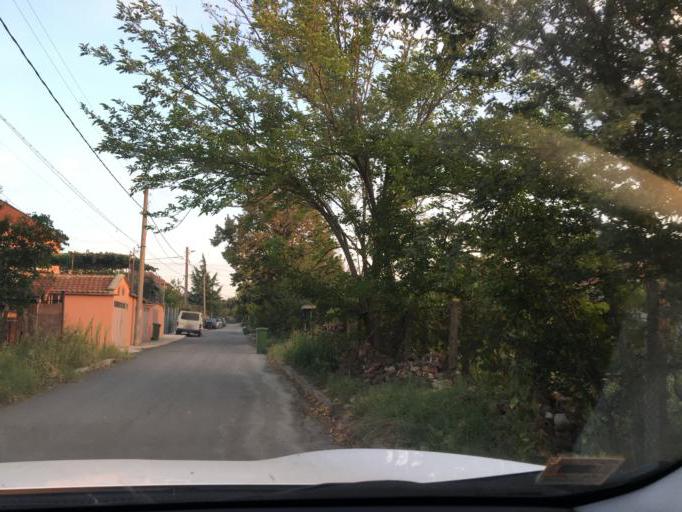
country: BG
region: Burgas
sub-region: Obshtina Burgas
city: Burgas
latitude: 42.6127
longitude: 27.4956
